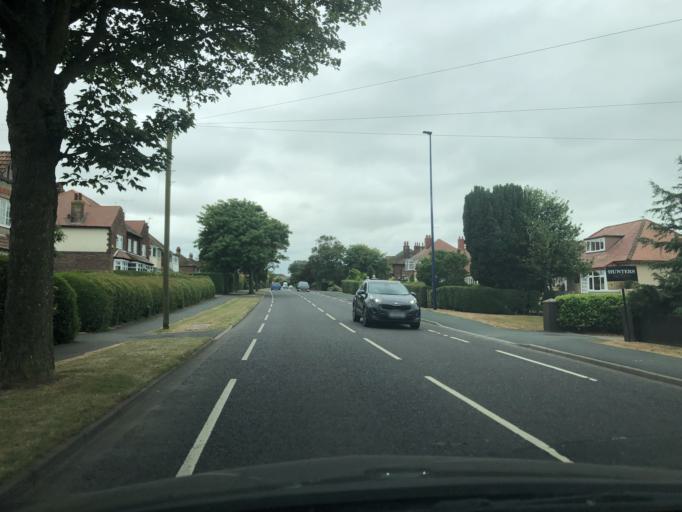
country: GB
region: England
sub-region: North Yorkshire
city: Filey
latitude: 54.2082
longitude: -0.2980
